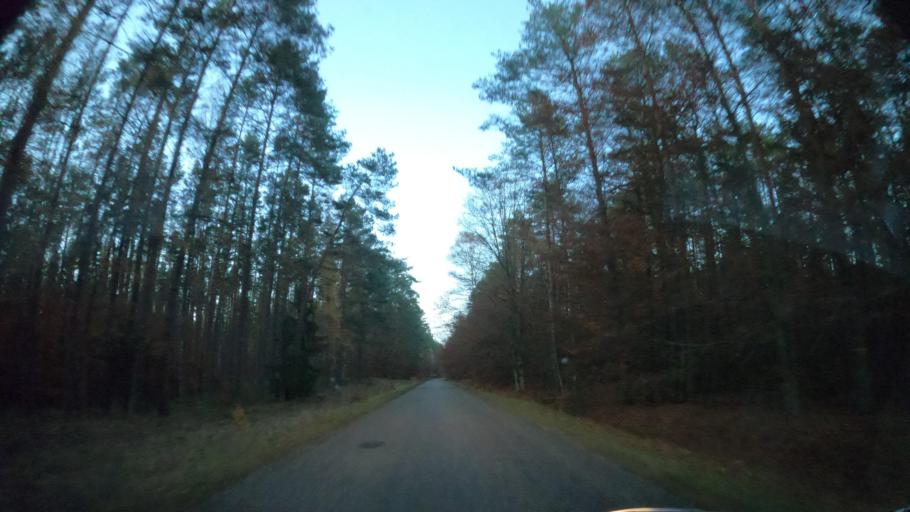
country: PL
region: Greater Poland Voivodeship
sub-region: Powiat zlotowski
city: Sypniewo
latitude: 53.3982
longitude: 16.5779
